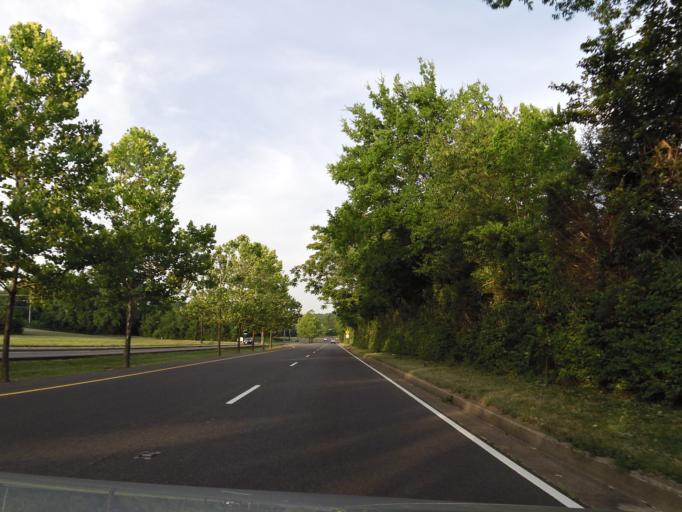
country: US
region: Tennessee
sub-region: Knox County
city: Knoxville
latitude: 35.9450
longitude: -84.0269
